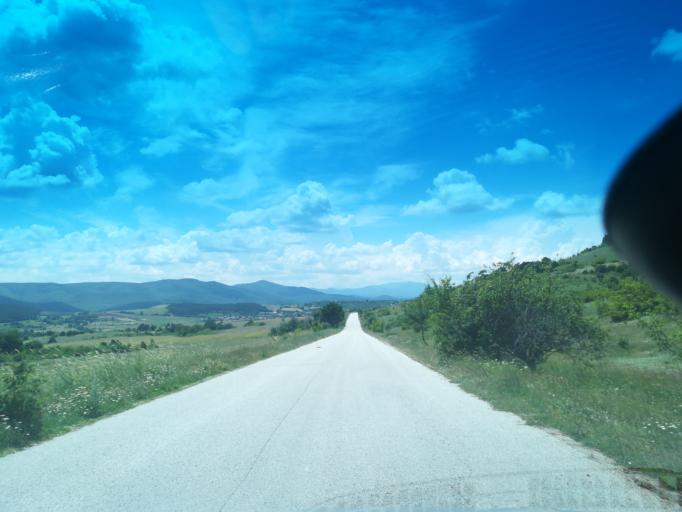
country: BG
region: Khaskovo
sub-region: Obshtina Mineralni Bani
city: Mineralni Bani
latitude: 41.9571
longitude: 25.2623
